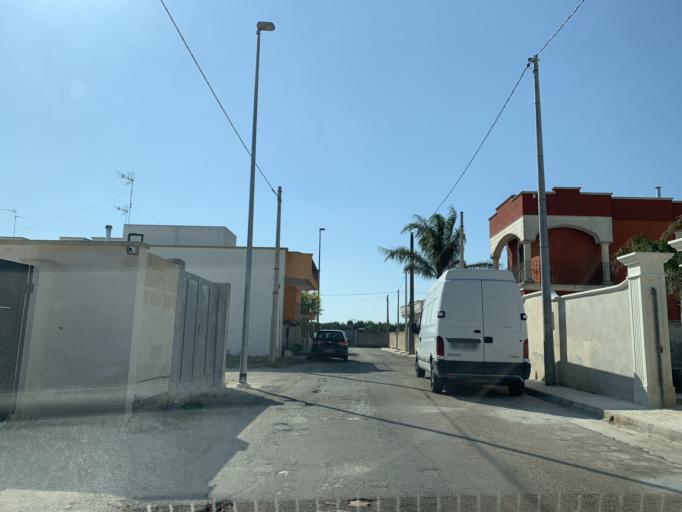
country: IT
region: Apulia
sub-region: Provincia di Lecce
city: Copertino
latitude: 40.2656
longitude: 18.0379
